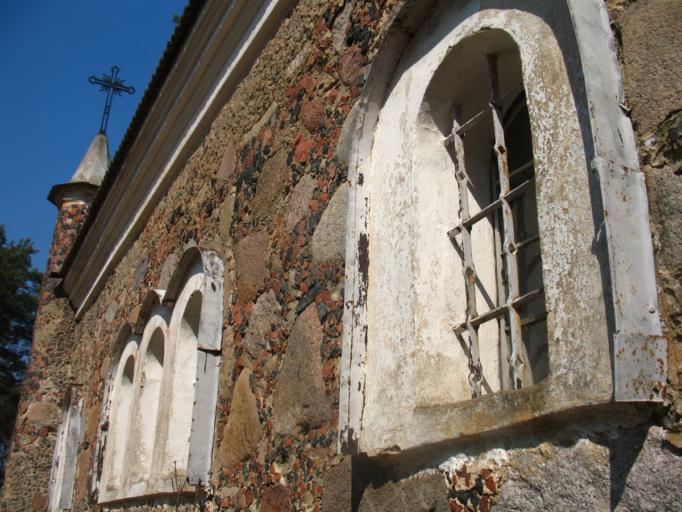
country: BY
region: Brest
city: Kosava
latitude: 52.7473
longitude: 25.1747
